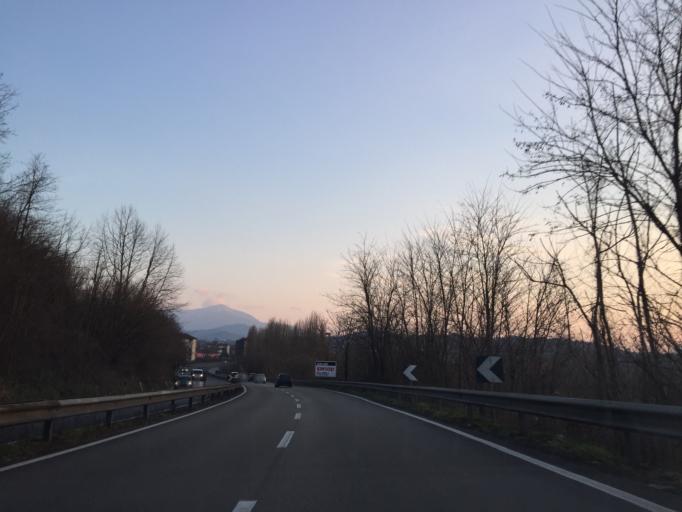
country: IT
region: Campania
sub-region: Provincia di Avellino
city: Atripalda
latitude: 40.9229
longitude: 14.8260
